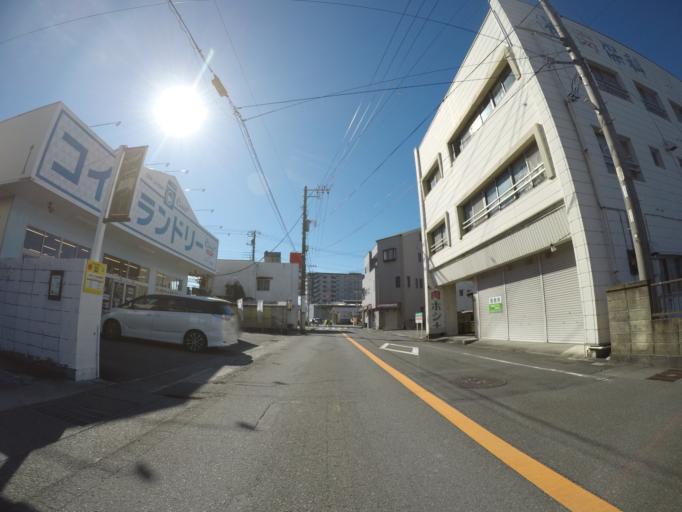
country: JP
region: Shizuoka
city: Fuji
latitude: 35.1654
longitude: 138.6959
